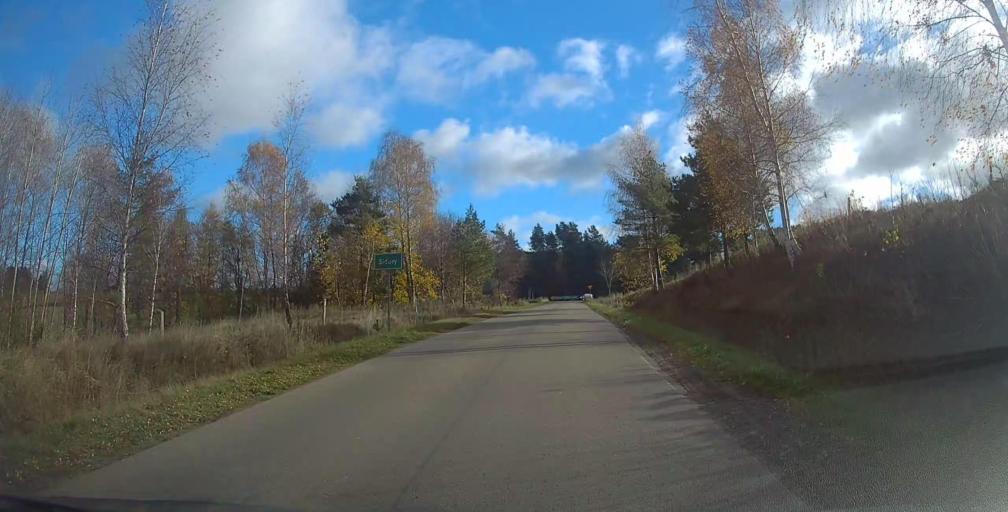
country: PL
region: Podlasie
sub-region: Suwalki
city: Suwalki
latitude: 54.2698
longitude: 22.9233
